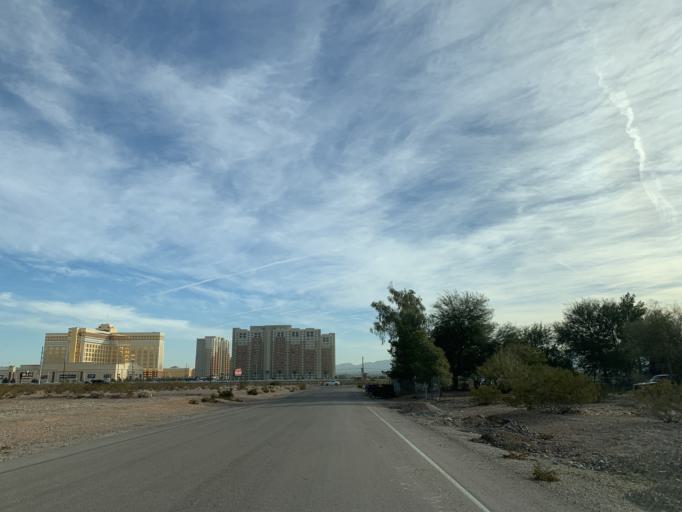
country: US
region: Nevada
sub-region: Clark County
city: Enterprise
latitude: 36.0080
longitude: -115.1849
